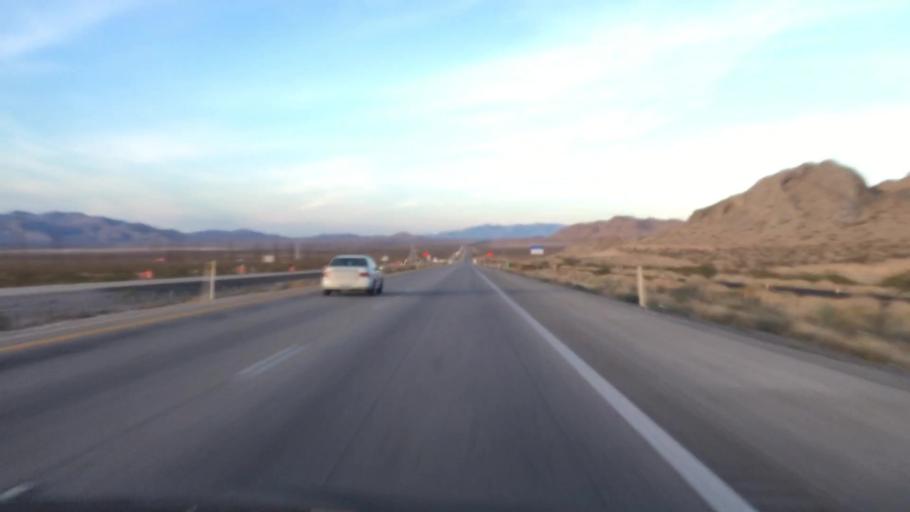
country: US
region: Nevada
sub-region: Clark County
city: Nellis Air Force Base
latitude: 36.3888
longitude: -114.8865
